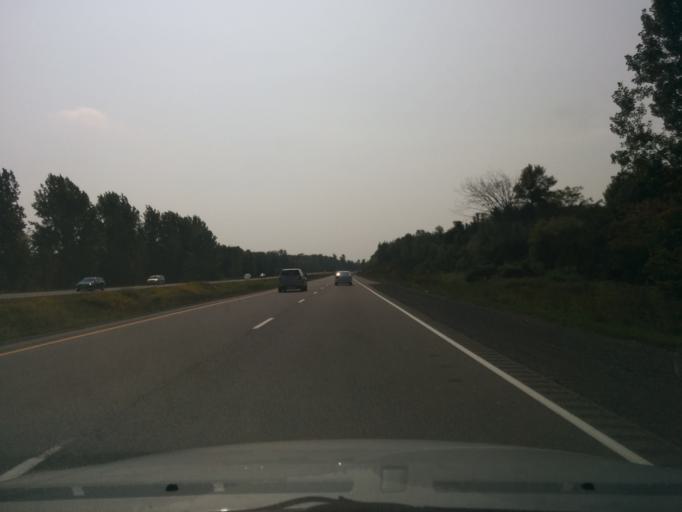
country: CA
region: Ontario
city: Bells Corners
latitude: 45.1376
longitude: -75.6773
